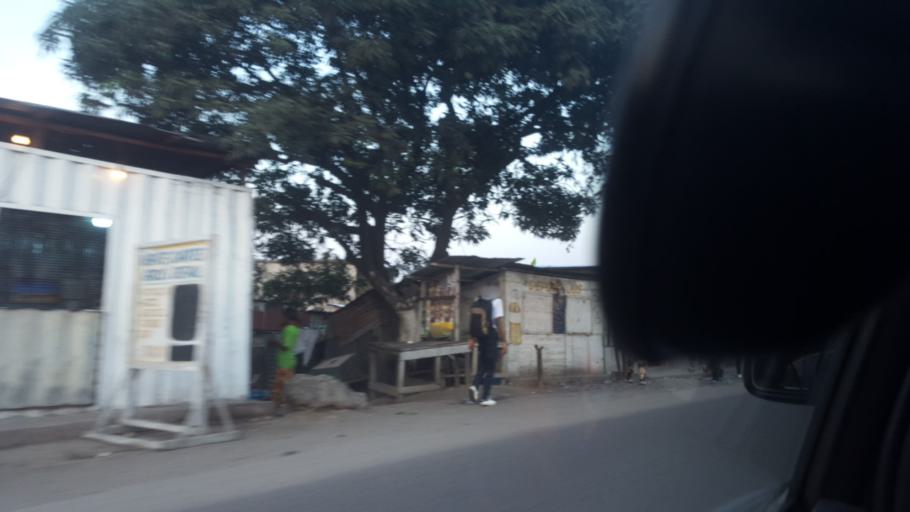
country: CD
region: Kinshasa
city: Kinshasa
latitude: -4.3511
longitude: 15.3261
